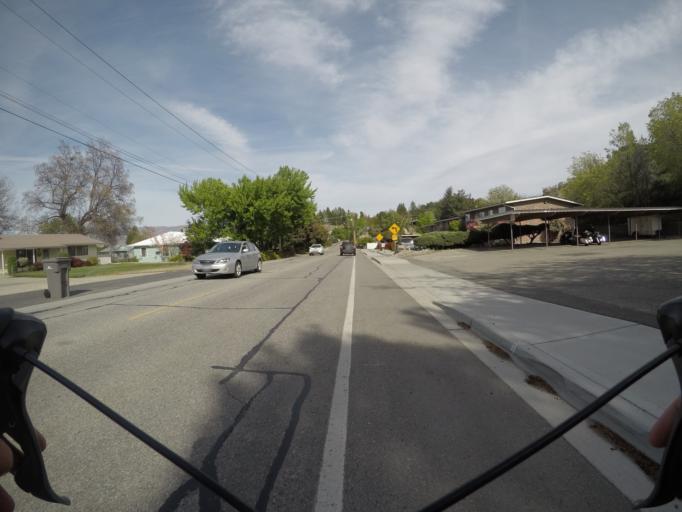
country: US
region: Washington
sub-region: Chelan County
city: West Wenatchee
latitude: 47.4136
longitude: -120.3477
